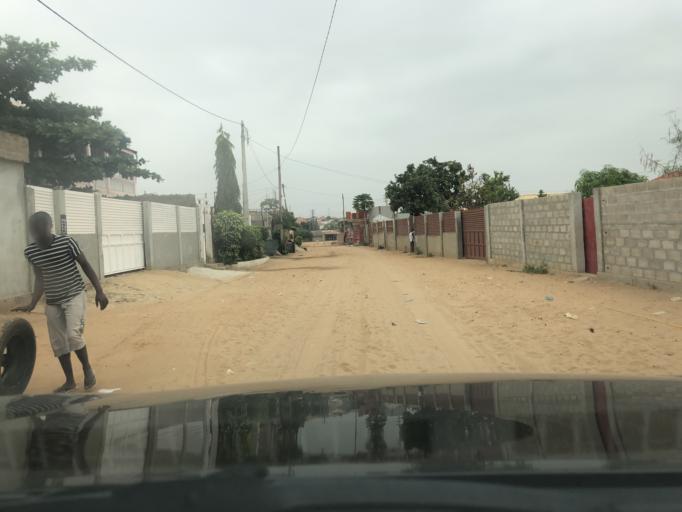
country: AO
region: Luanda
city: Luanda
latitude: -8.9387
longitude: 13.2380
